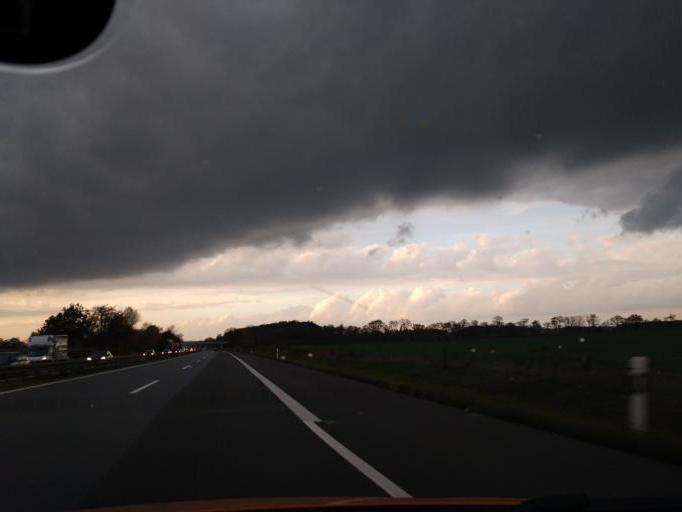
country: DE
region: Brandenburg
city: Triglitz
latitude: 53.2653
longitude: 12.1389
